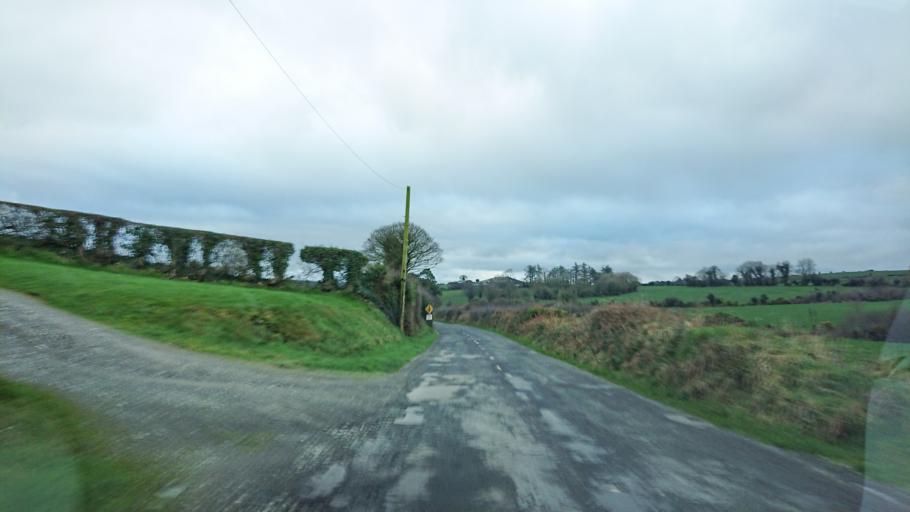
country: IE
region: Munster
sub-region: Waterford
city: Portlaw
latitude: 52.2424
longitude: -7.4161
